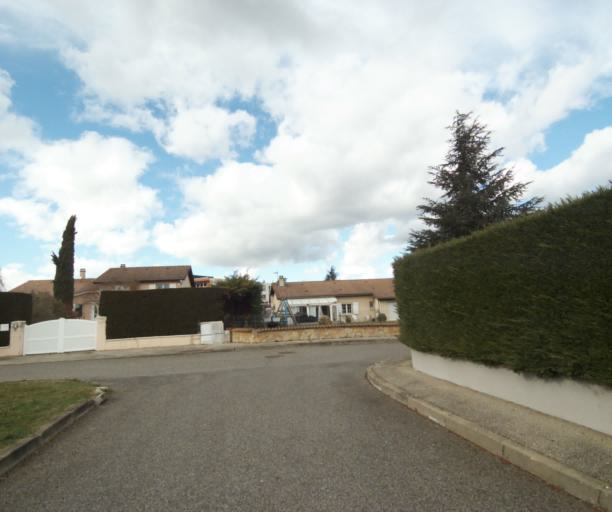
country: FR
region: Rhone-Alpes
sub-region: Departement de la Loire
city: La Talaudiere
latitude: 45.4662
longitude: 4.4164
